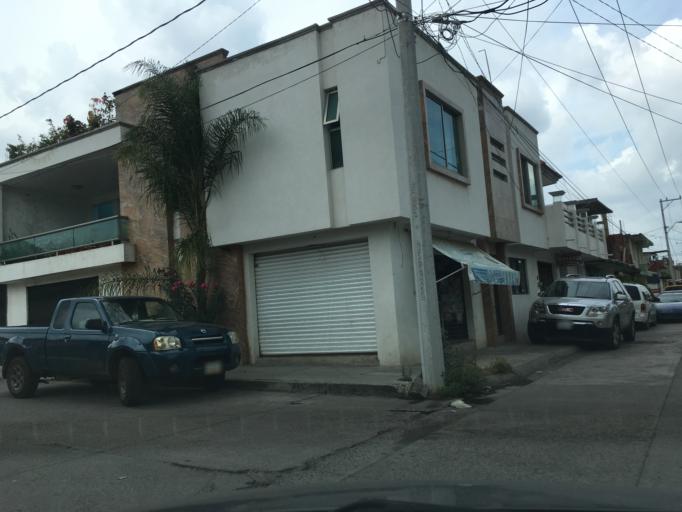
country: MX
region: Michoacan
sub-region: Uruapan
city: Uruapan
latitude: 19.4150
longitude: -102.0717
